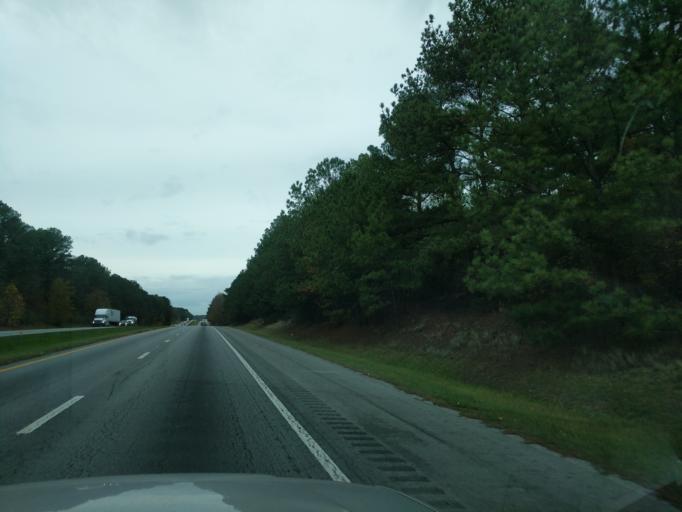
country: US
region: South Carolina
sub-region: Laurens County
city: Joanna
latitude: 34.4276
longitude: -81.7275
